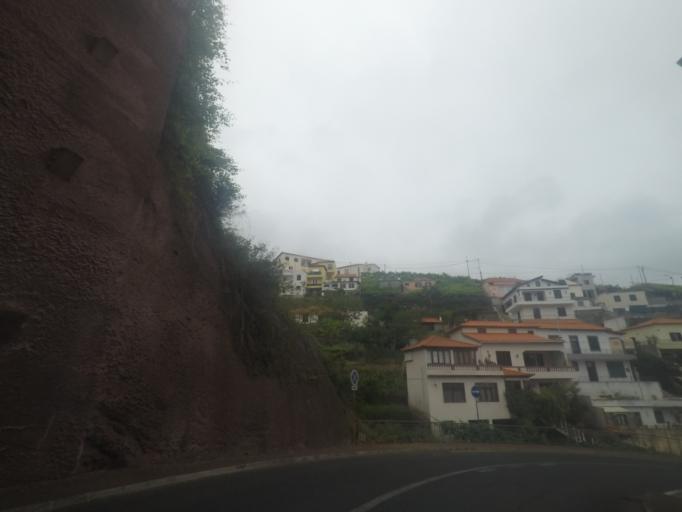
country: PT
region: Madeira
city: Camara de Lobos
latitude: 32.6747
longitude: -16.9791
